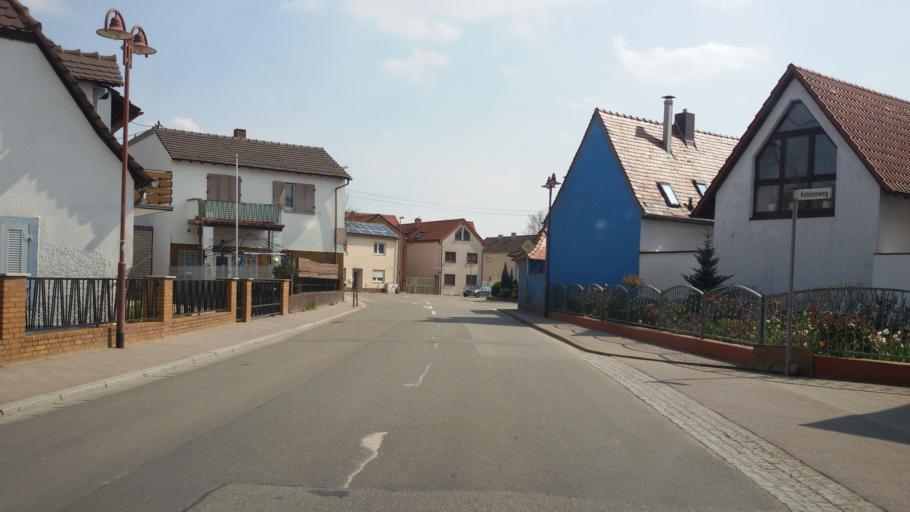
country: DE
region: Rheinland-Pfalz
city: Hessheim
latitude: 49.5481
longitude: 8.3071
